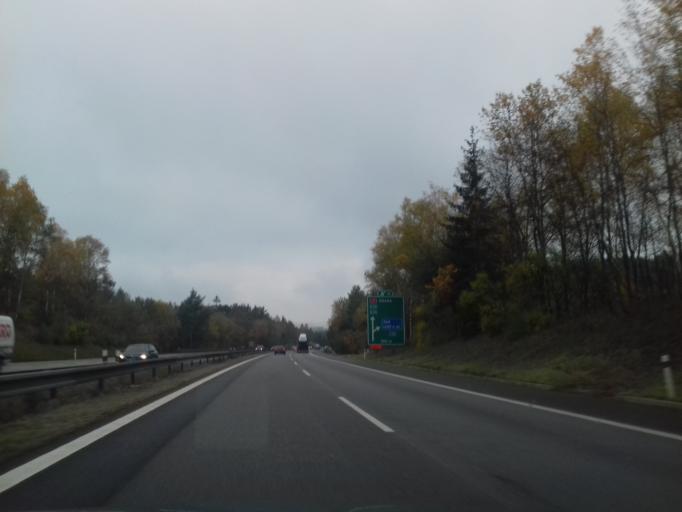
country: CZ
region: Vysocina
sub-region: Okres Pelhrimov
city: Zeliv
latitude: 49.5713
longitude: 15.2746
